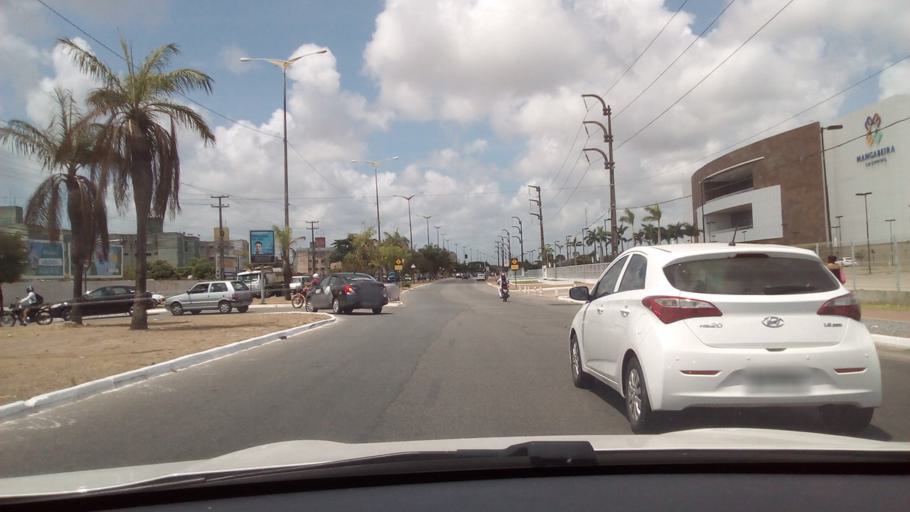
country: BR
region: Paraiba
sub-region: Joao Pessoa
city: Joao Pessoa
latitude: -7.1635
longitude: -34.8290
